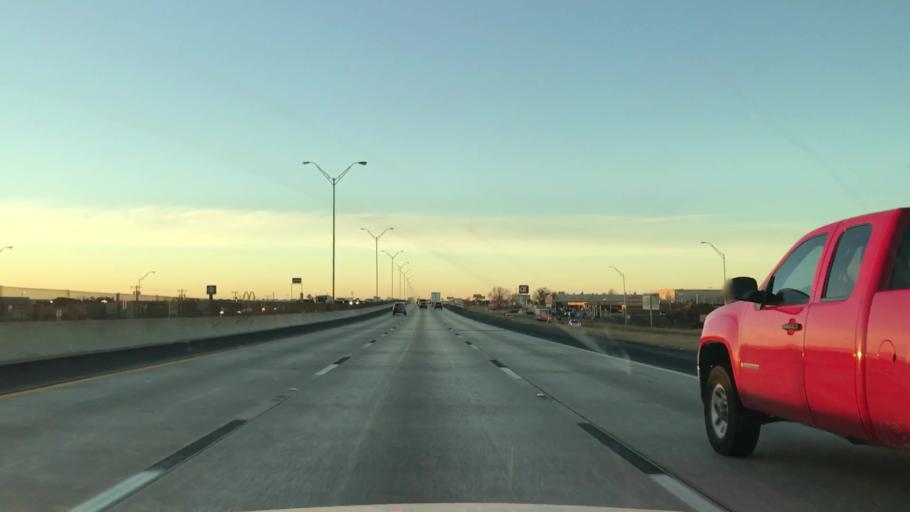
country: US
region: Texas
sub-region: Tarrant County
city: Everman
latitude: 32.6313
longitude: -97.3217
